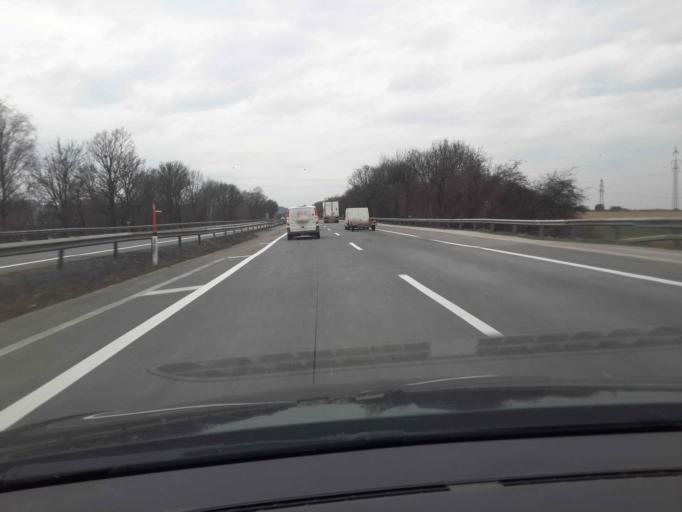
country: AT
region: Lower Austria
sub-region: Politischer Bezirk Melk
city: Leiben
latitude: 48.2108
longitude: 15.2785
